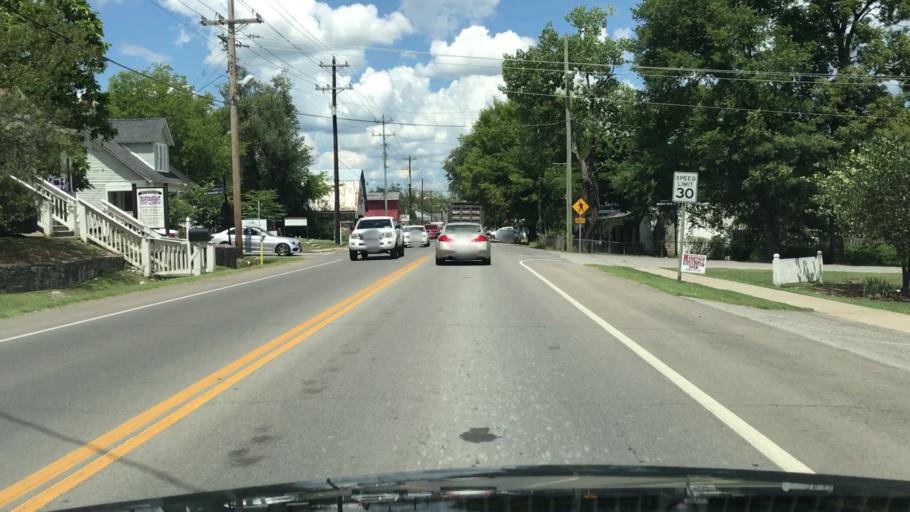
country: US
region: Tennessee
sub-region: Williamson County
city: Nolensville
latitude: 35.9519
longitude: -86.6691
